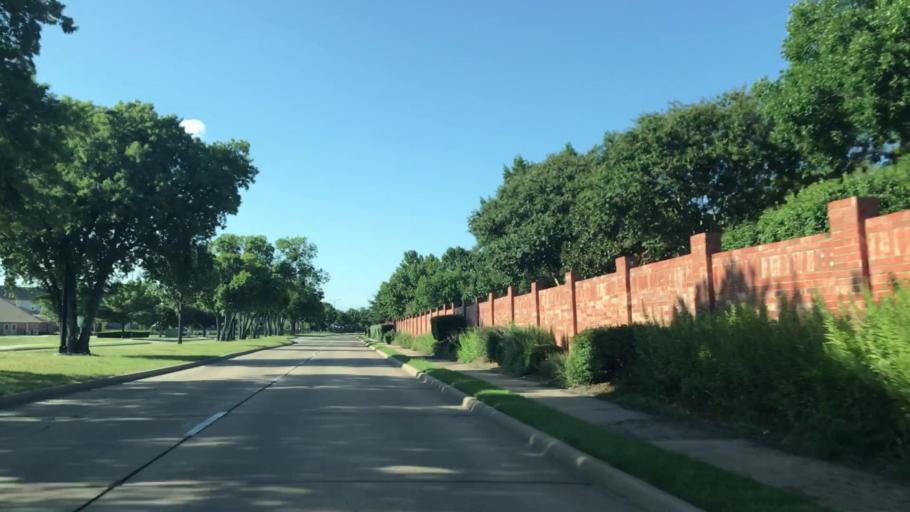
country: US
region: Texas
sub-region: Collin County
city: Frisco
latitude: 33.1262
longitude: -96.7878
